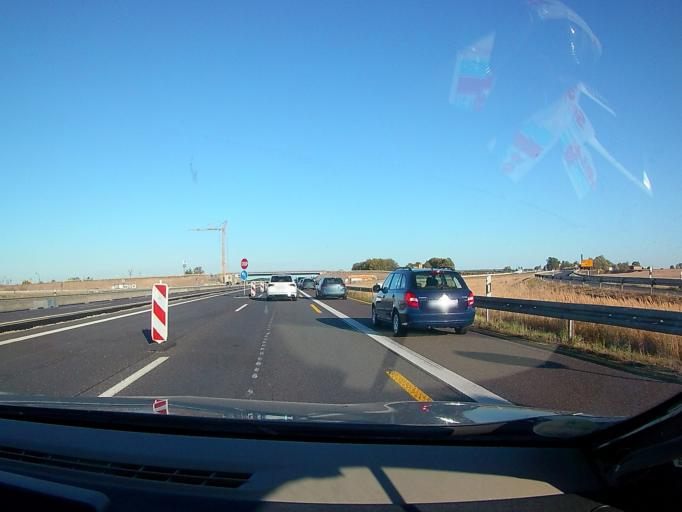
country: DE
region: Brandenburg
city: Velten
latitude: 52.7067
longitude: 13.1012
